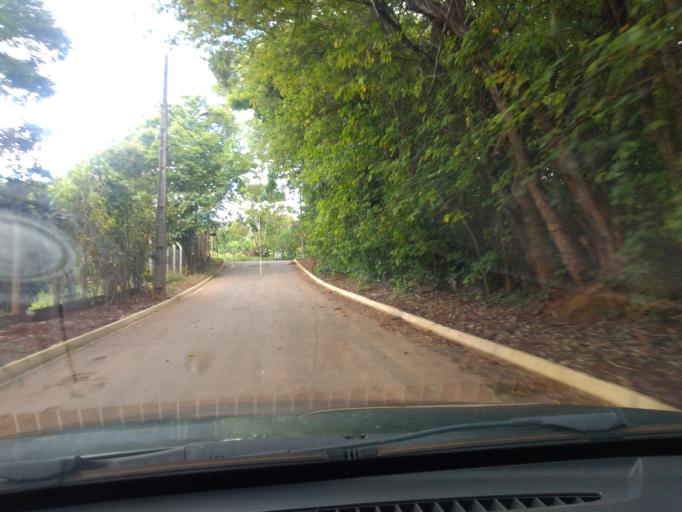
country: BR
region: Minas Gerais
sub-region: Tres Coracoes
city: Tres Coracoes
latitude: -21.6873
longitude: -45.2691
